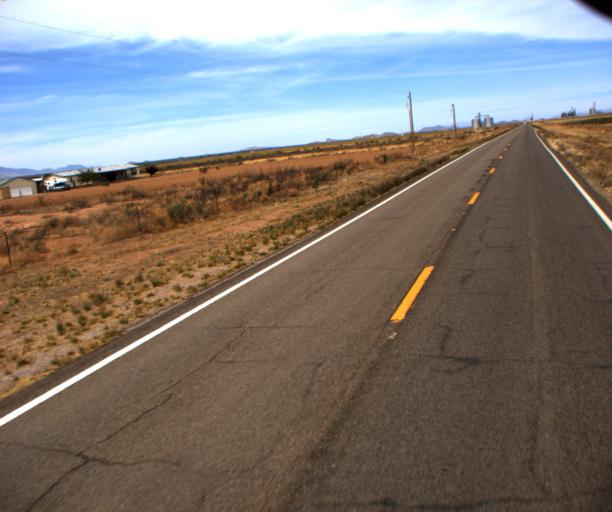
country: US
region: Arizona
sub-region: Cochise County
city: Tombstone
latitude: 31.7445
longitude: -109.6883
